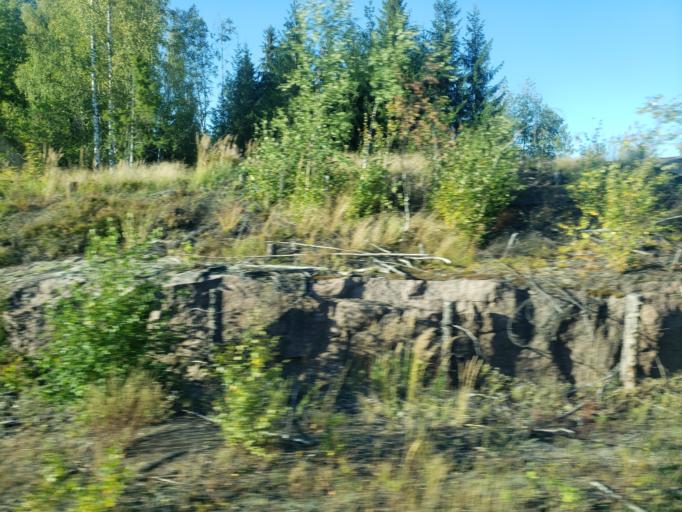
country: FI
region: South Karelia
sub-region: Lappeenranta
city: Lappeenranta
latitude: 60.9077
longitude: 28.1465
